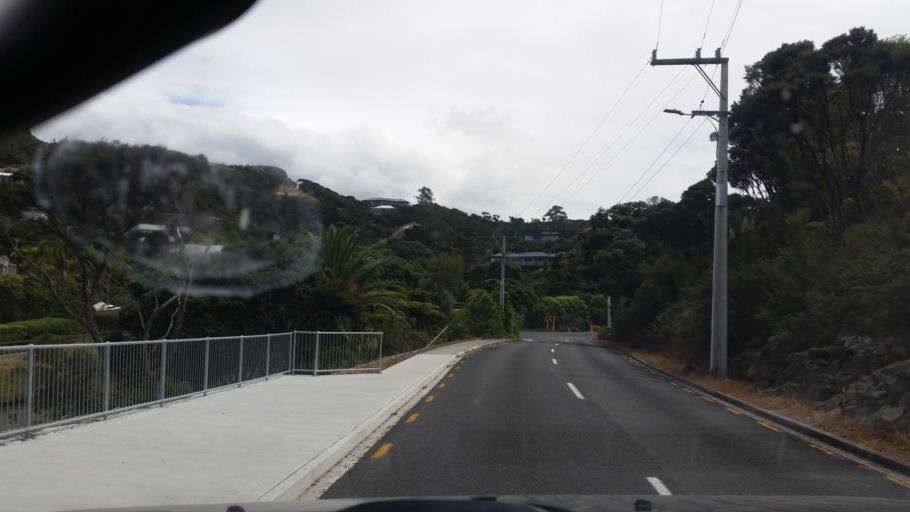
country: NZ
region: Auckland
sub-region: Auckland
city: Wellsford
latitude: -36.0822
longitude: 174.5907
